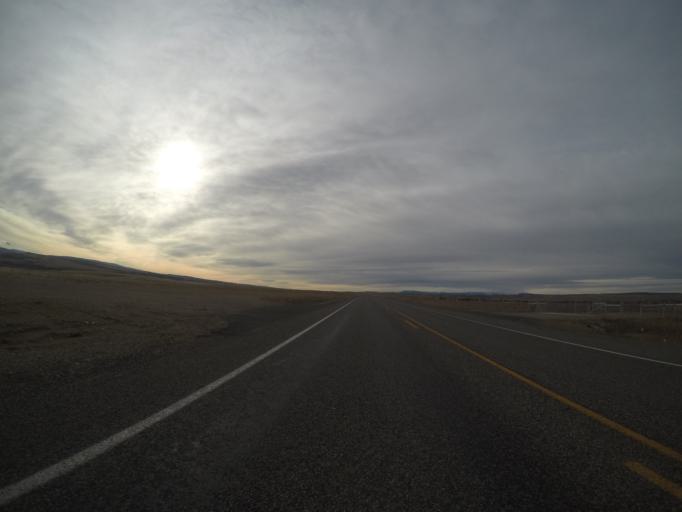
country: US
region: Montana
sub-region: Yellowstone County
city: Laurel
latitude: 45.5779
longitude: -108.8439
